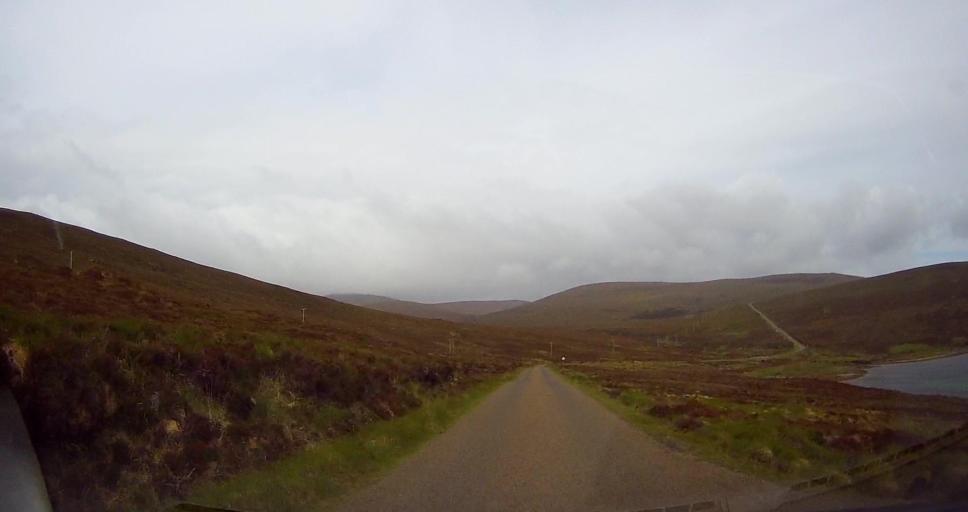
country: GB
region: Scotland
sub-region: Orkney Islands
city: Stromness
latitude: 58.8682
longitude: -3.2267
